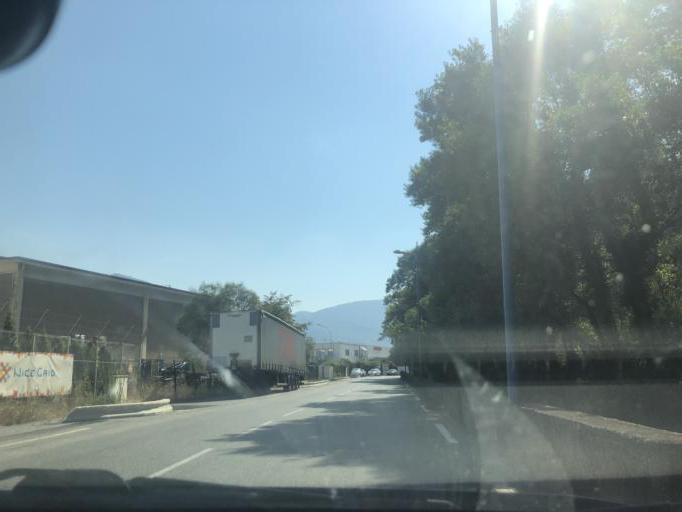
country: FR
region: Provence-Alpes-Cote d'Azur
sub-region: Departement des Alpes-Maritimes
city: Carros
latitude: 43.8021
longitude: 7.1911
